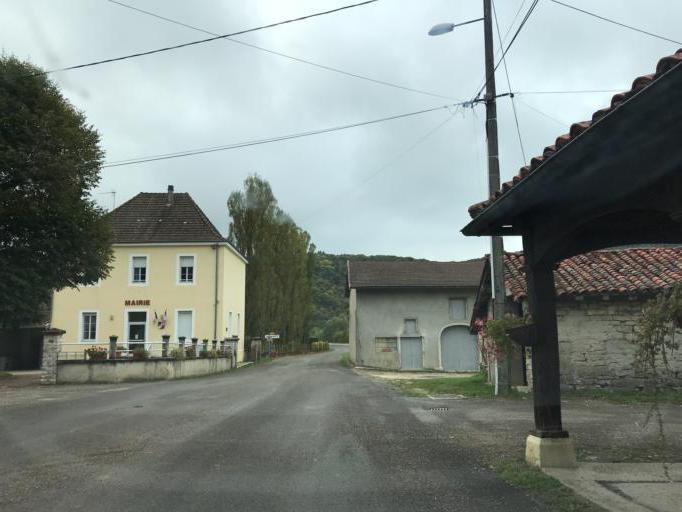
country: FR
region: Rhone-Alpes
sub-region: Departement de l'Ain
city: Cuisiat
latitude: 46.3736
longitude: 5.4402
